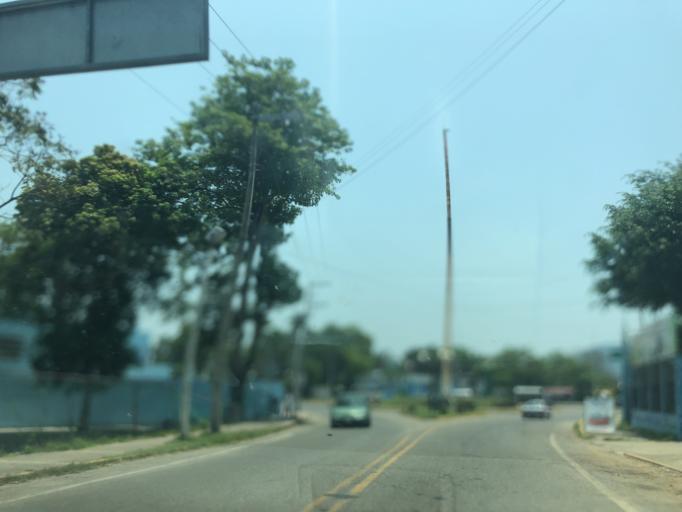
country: MX
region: Tabasco
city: Teapa
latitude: 17.5690
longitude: -92.9565
